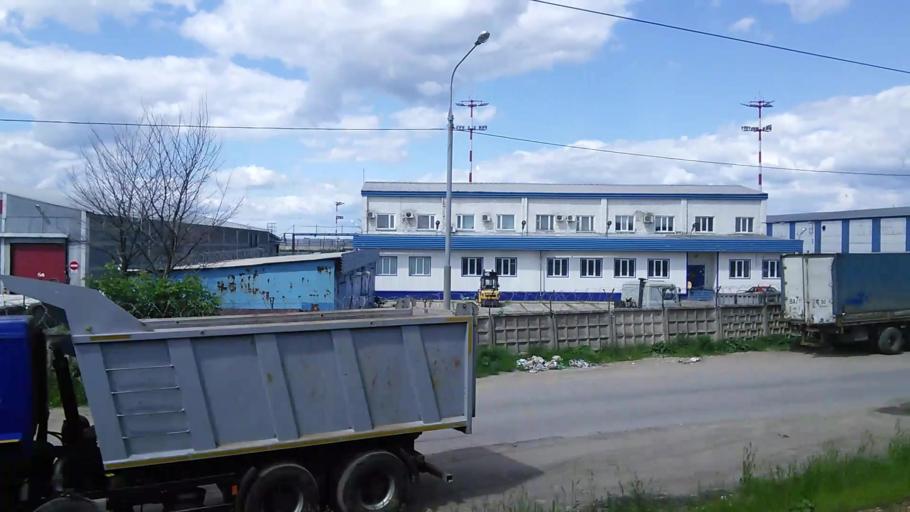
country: RU
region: Moskovskaya
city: Sheremet'yevskiy
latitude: 55.9702
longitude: 37.4430
